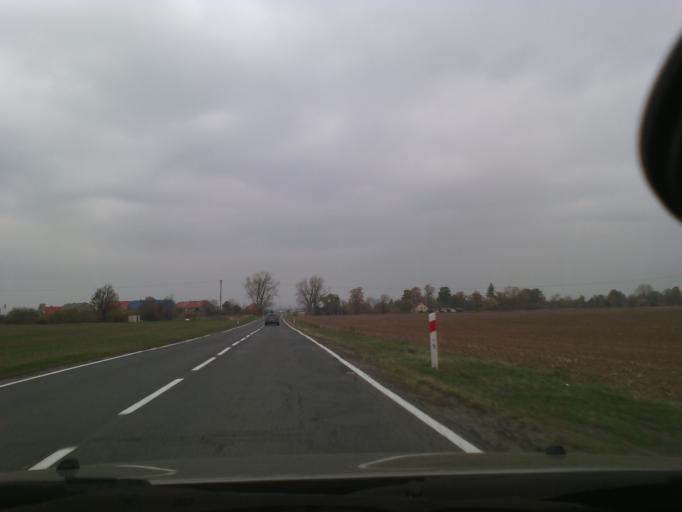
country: PL
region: Lower Silesian Voivodeship
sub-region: Powiat walbrzyski
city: Stare Bogaczowice
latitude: 50.9089
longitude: 16.2508
